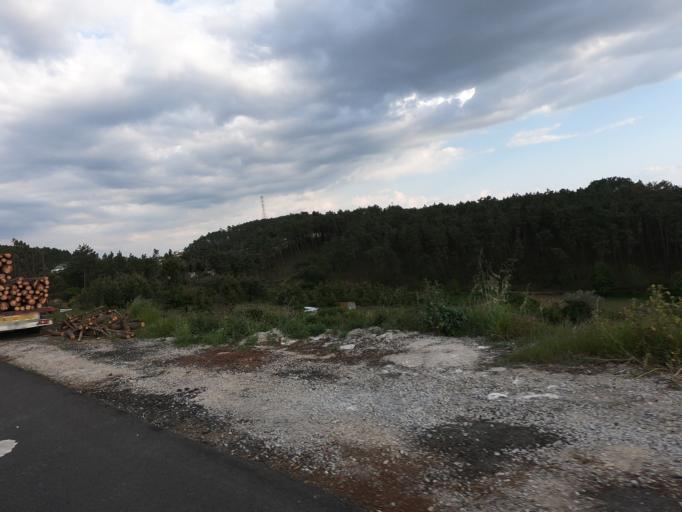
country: PT
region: Vila Real
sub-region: Sabrosa
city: Vilela
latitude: 41.2212
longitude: -7.6777
